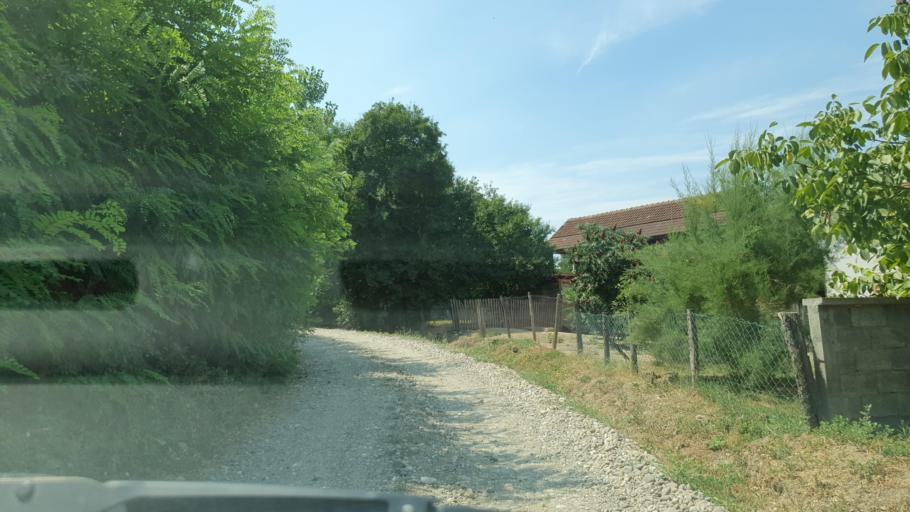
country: BA
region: Republika Srpska
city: Bijeljina
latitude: 44.7222
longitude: 19.1915
